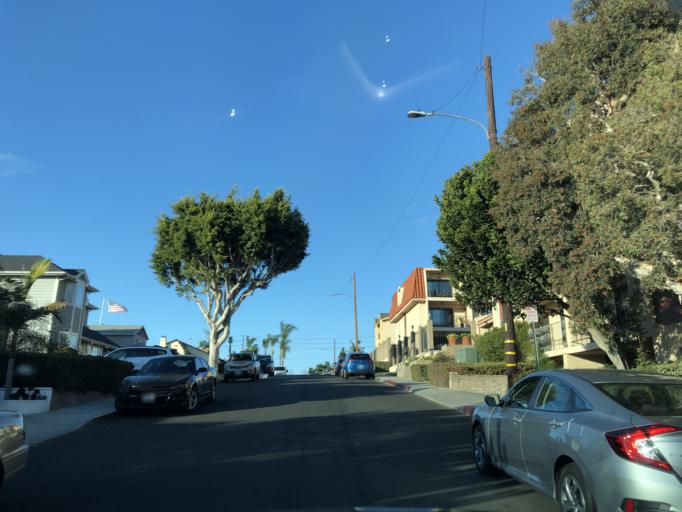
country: US
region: California
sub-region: Los Angeles County
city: El Segundo
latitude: 33.9292
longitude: -118.4170
